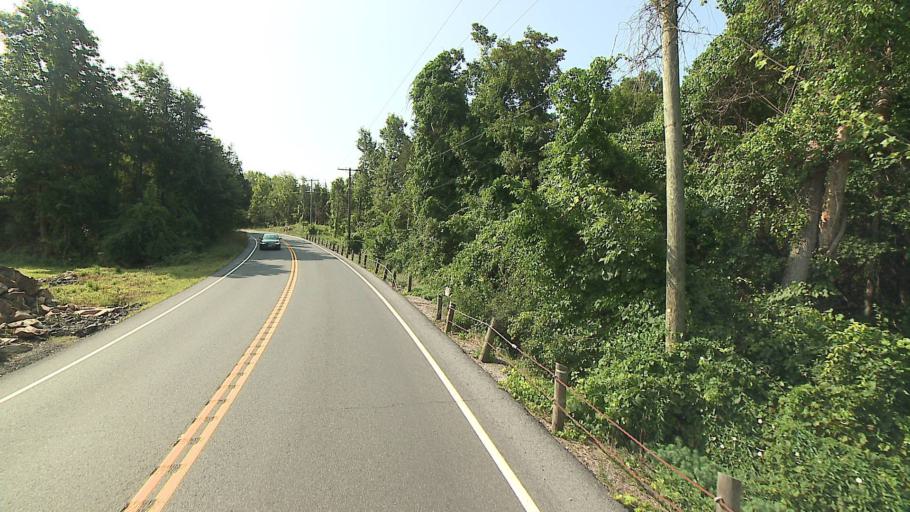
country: US
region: Connecticut
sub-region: Litchfield County
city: Kent
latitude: 41.6671
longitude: -73.5022
